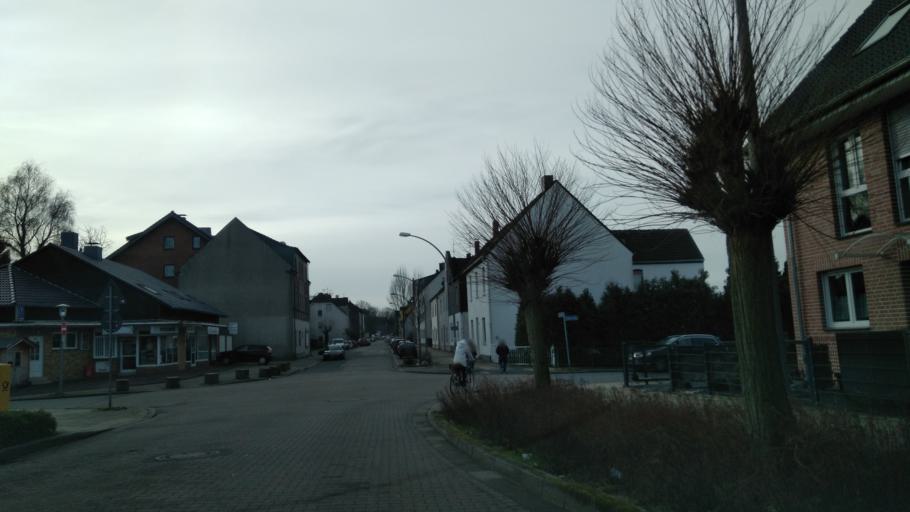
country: DE
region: North Rhine-Westphalia
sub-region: Regierungsbezirk Munster
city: Gladbeck
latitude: 51.5852
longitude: 7.0002
